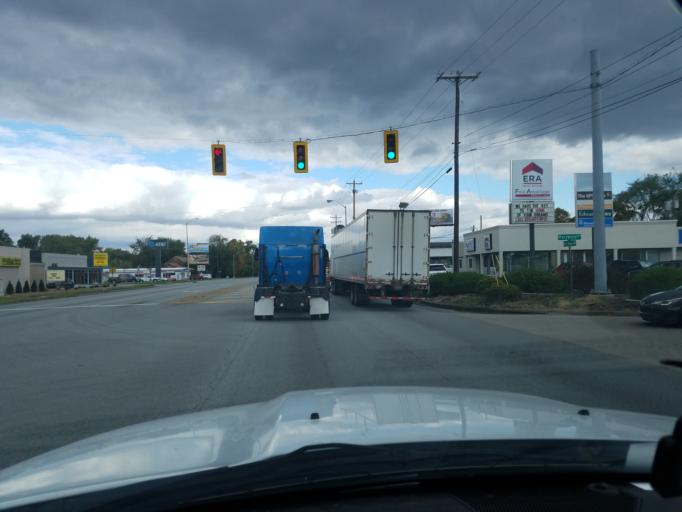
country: US
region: Kentucky
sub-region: Henderson County
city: Henderson
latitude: 37.8672
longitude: -87.5722
